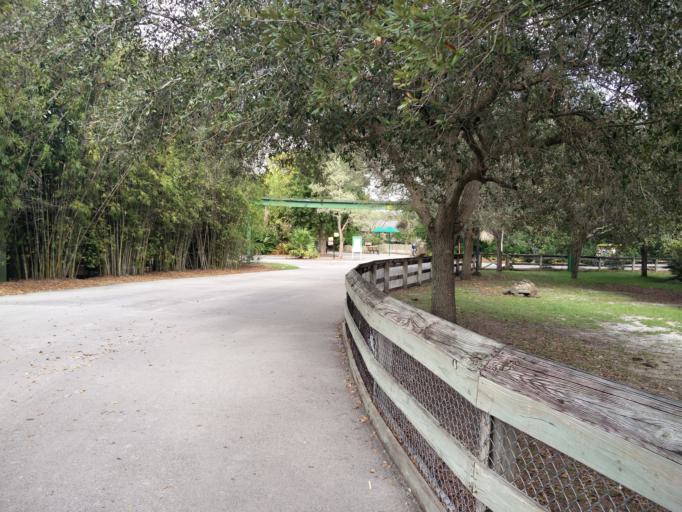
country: US
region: Florida
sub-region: Miami-Dade County
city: South Miami Heights
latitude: 25.6086
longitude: -80.3977
